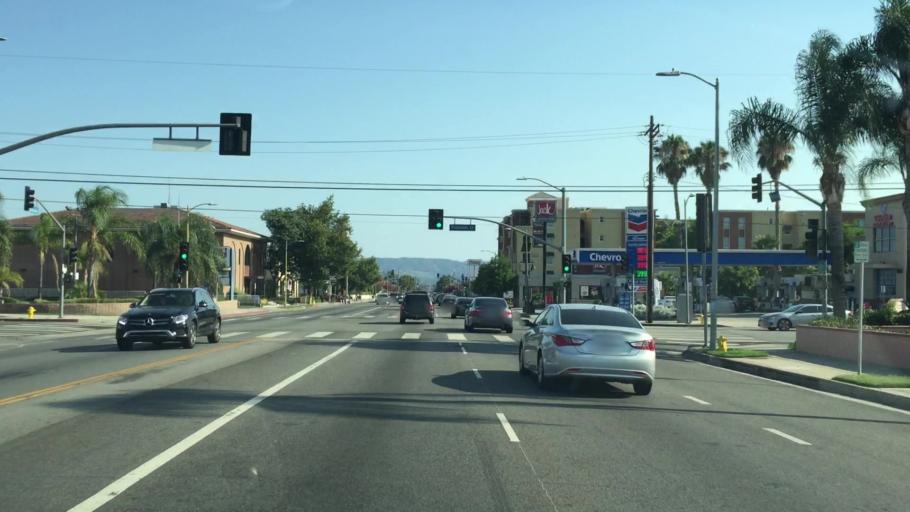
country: US
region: California
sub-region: Los Angeles County
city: Northridge
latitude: 34.2431
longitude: -118.5361
